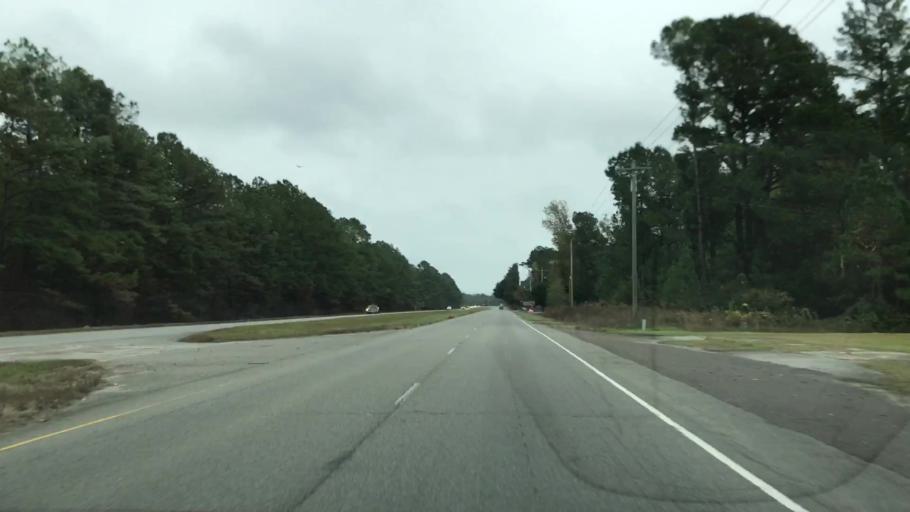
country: US
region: South Carolina
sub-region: Charleston County
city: Awendaw
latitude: 33.0381
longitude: -79.6066
